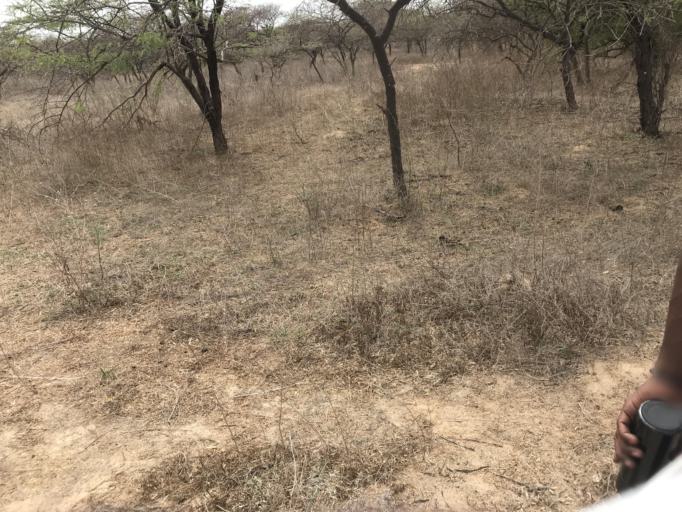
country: SN
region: Saint-Louis
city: Saint-Louis
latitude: 15.9104
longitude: -16.4561
